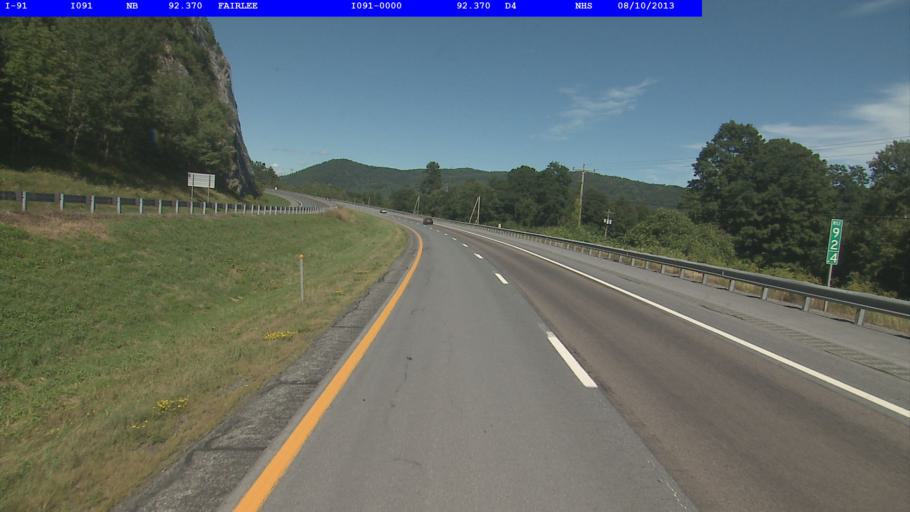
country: US
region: New Hampshire
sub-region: Grafton County
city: Orford
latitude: 43.9106
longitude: -72.1373
